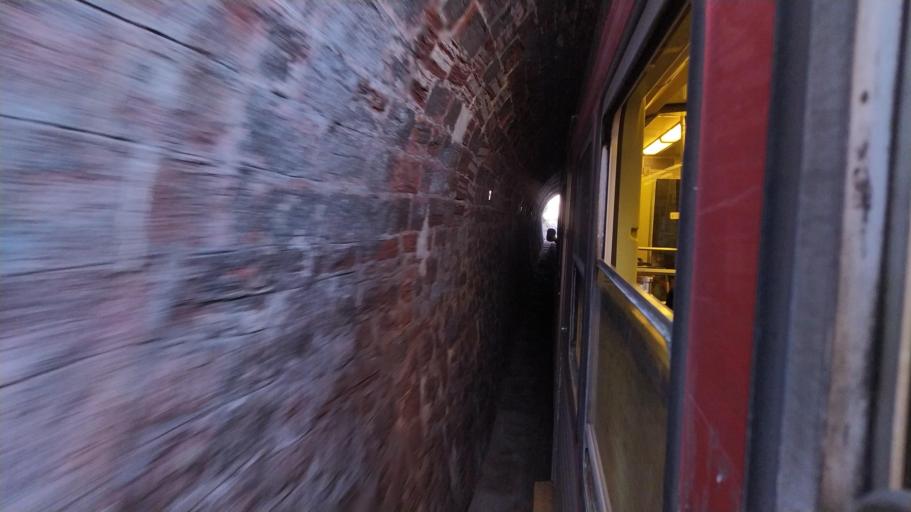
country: PT
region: Aveiro
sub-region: Aveiro
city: Eixo
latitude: 40.6079
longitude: -8.5305
